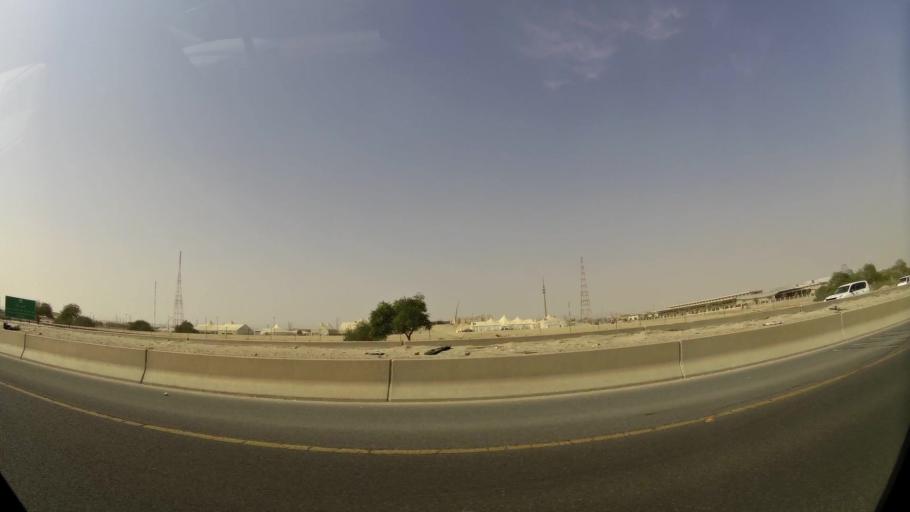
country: KW
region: Al Ahmadi
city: Al Fahahil
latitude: 29.0844
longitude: 48.1148
